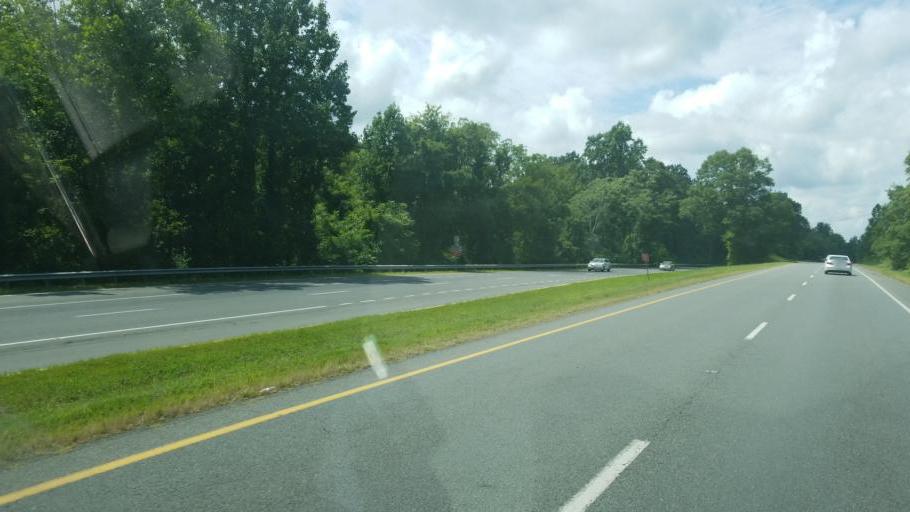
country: US
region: Virginia
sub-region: Fauquier County
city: Warrenton
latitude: 38.7667
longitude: -77.8158
